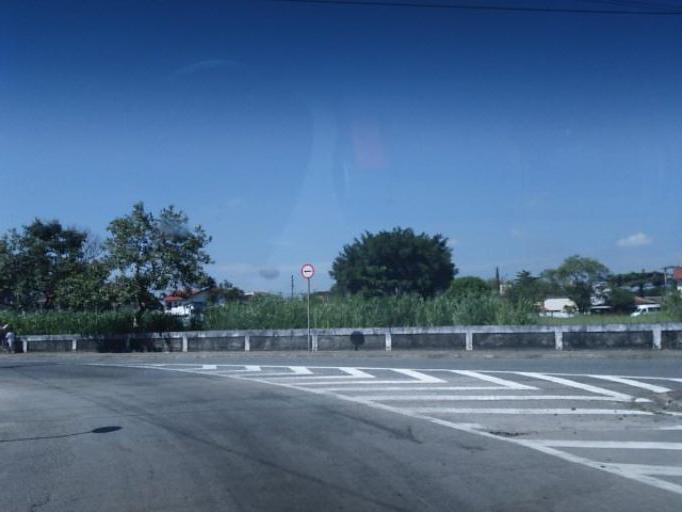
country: BR
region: Sao Paulo
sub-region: Sao Jose Dos Campos
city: Sao Jose dos Campos
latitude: -23.1962
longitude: -45.8815
